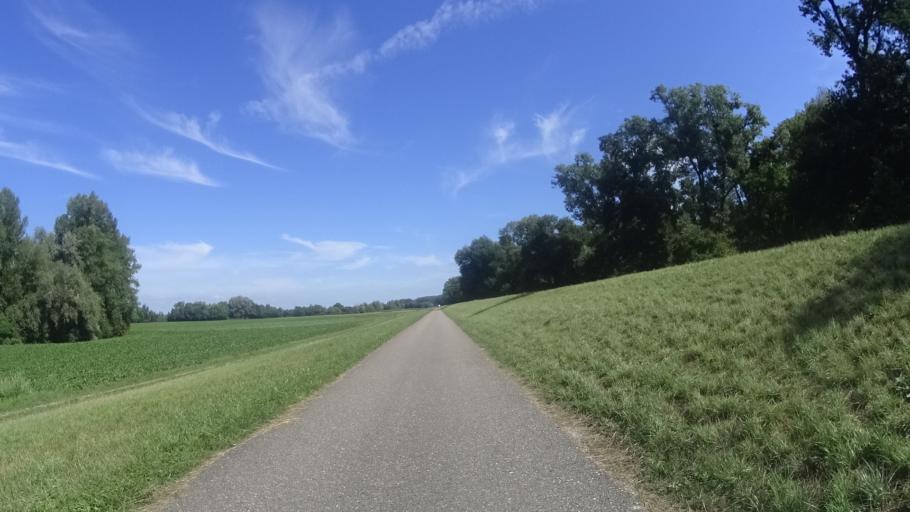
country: DE
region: Rheinland-Pfalz
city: Leimersheim
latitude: 49.1094
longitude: 8.3520
